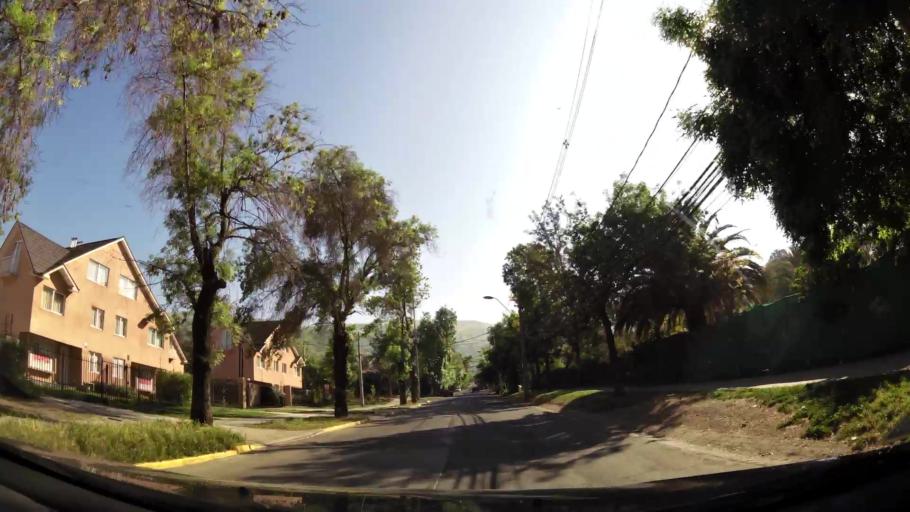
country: CL
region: Santiago Metropolitan
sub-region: Provincia de Chacabuco
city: Chicureo Abajo
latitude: -33.3428
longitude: -70.6691
